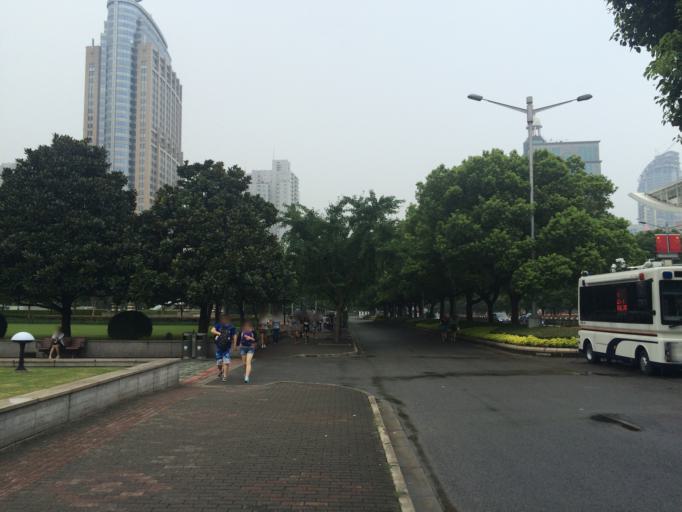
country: CN
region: Shanghai Shi
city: Shanghai
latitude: 31.2315
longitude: 121.4694
